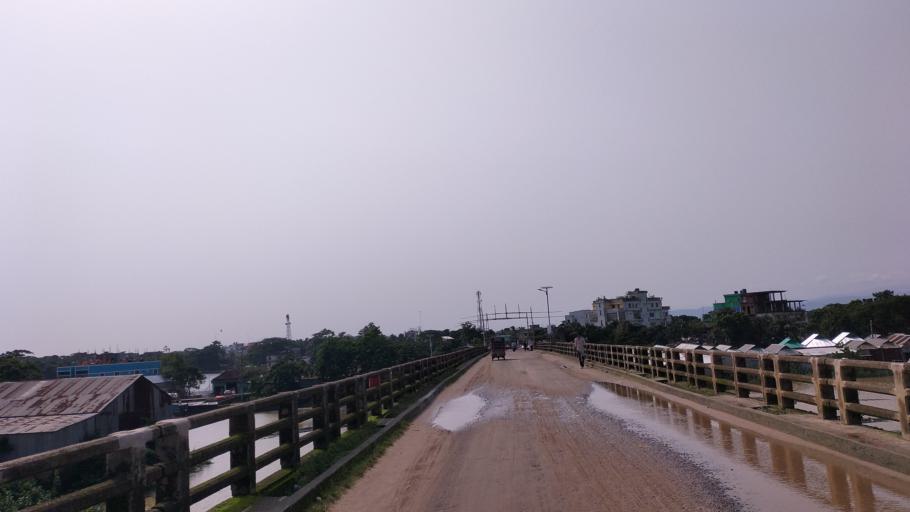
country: BD
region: Dhaka
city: Netrakona
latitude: 25.0749
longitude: 90.8906
